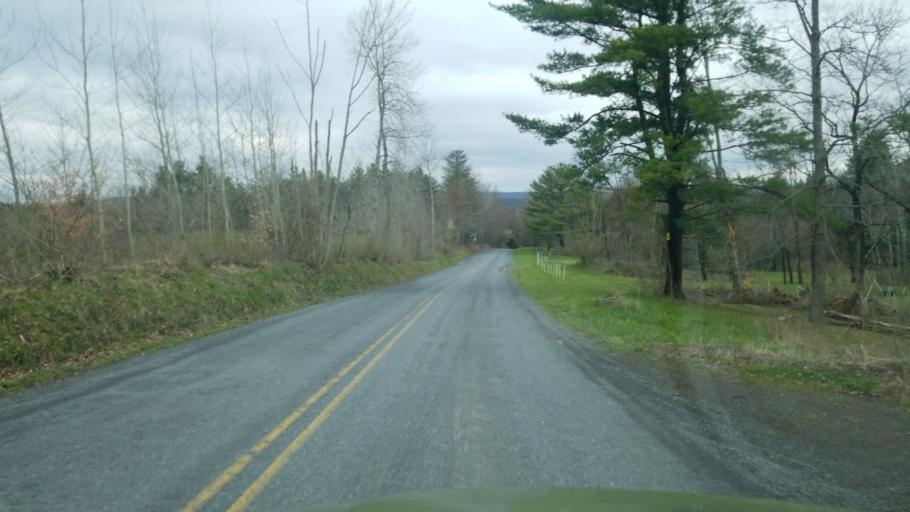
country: US
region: Pennsylvania
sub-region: Clearfield County
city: Clearfield
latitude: 41.0573
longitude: -78.4272
